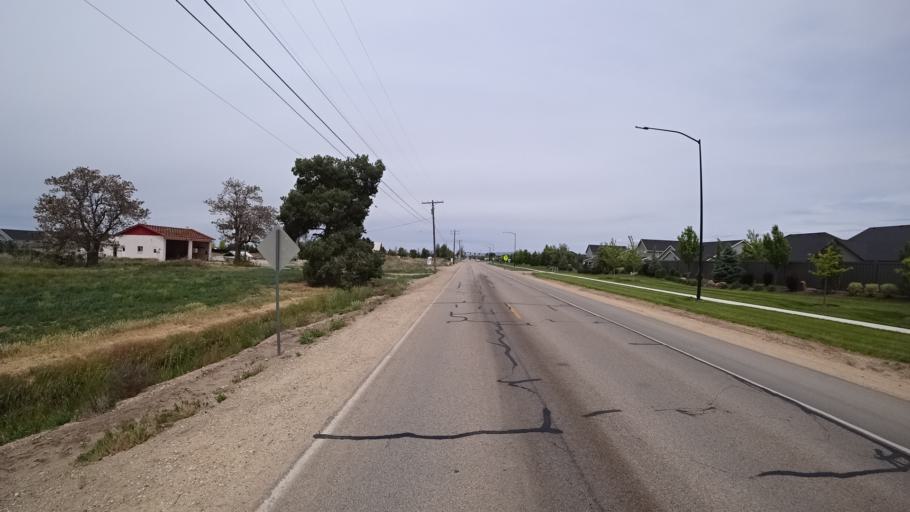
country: US
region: Idaho
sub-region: Ada County
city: Meridian
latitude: 43.5512
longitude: -116.3544
